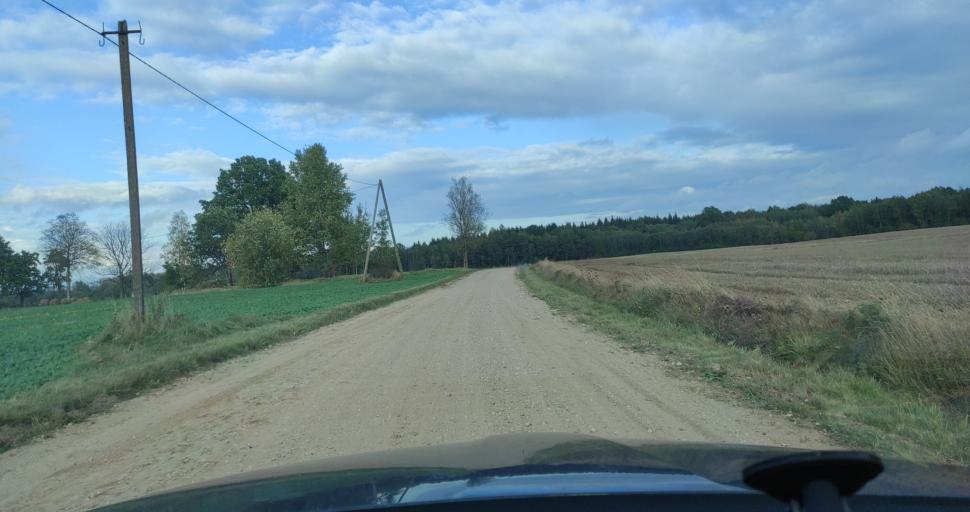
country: LV
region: Talsu Rajons
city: Sabile
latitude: 56.8995
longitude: 22.4290
